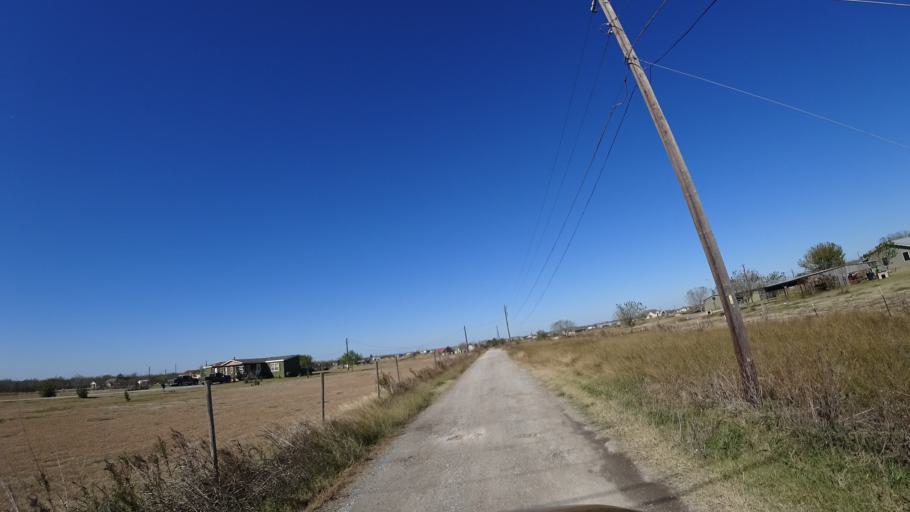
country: US
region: Texas
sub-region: Travis County
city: Garfield
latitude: 30.0977
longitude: -97.6175
